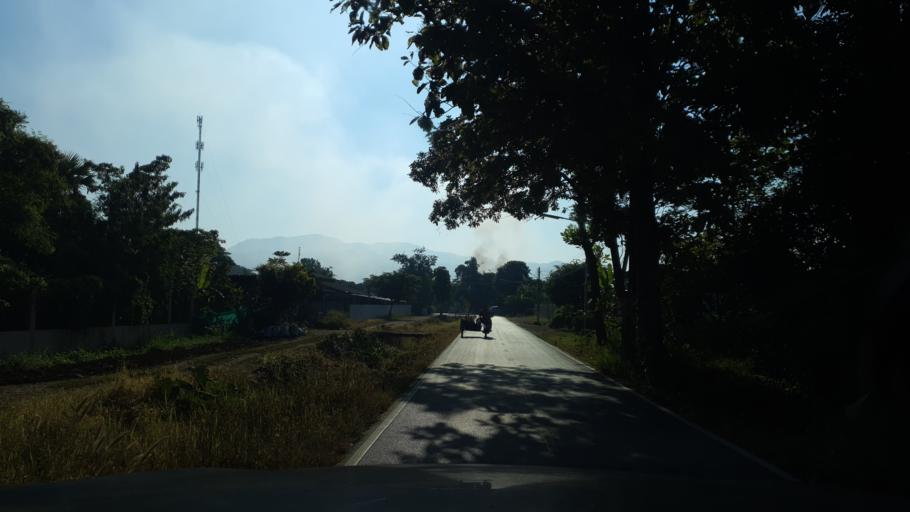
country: TH
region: Chiang Mai
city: San Kamphaeng
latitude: 18.6926
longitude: 99.1543
